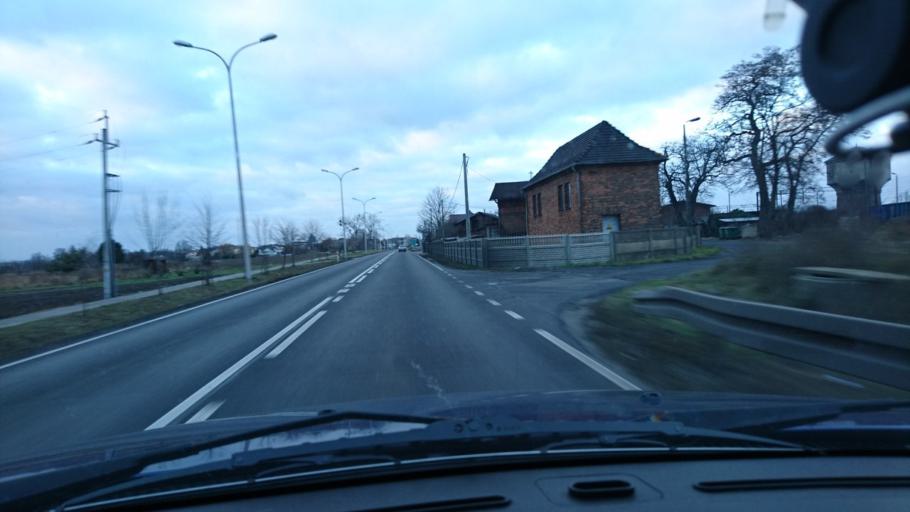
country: PL
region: Greater Poland Voivodeship
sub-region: Powiat kepinski
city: Kepno
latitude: 51.3017
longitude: 17.9943
